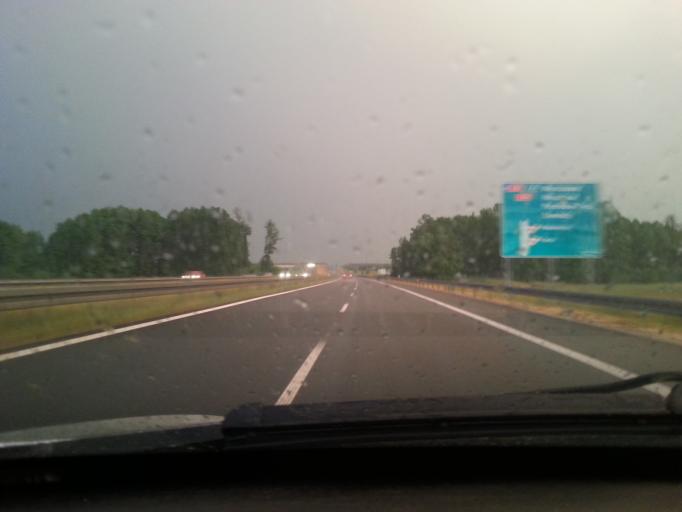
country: PL
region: Lodz Voivodeship
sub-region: Powiat pabianicki
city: Dobron
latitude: 51.6479
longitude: 19.2708
